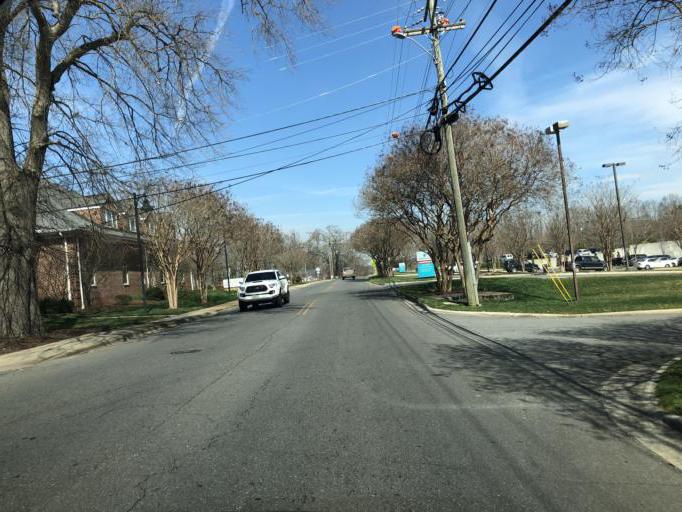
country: US
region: North Carolina
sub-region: Cleveland County
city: Shelby
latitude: 35.3025
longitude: -81.5379
